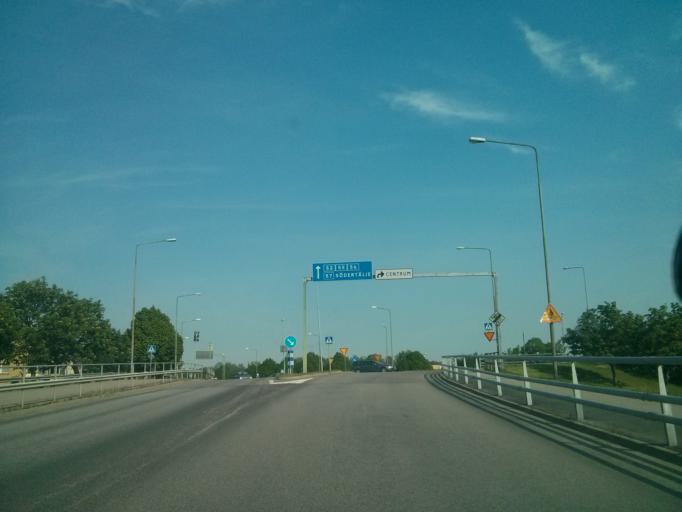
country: SE
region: Soedermanland
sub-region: Katrineholms Kommun
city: Katrineholm
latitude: 58.9970
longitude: 16.2119
